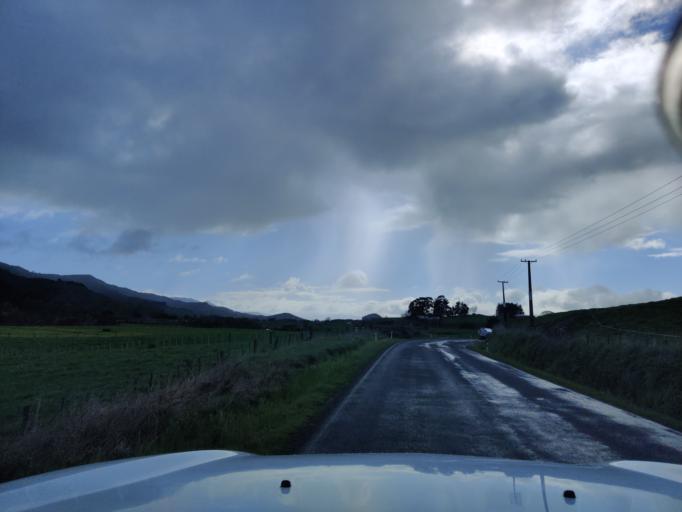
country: NZ
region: Waikato
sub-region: Waikato District
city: Ngaruawahia
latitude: -37.5907
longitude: 175.2108
